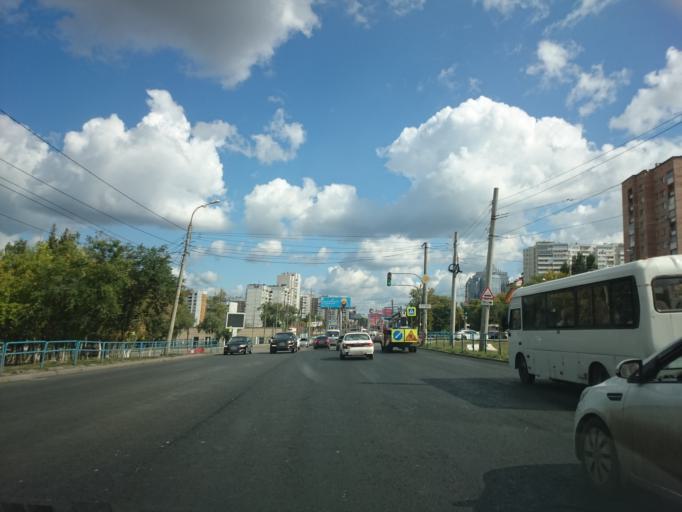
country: RU
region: Samara
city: Samara
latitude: 53.2338
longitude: 50.1854
